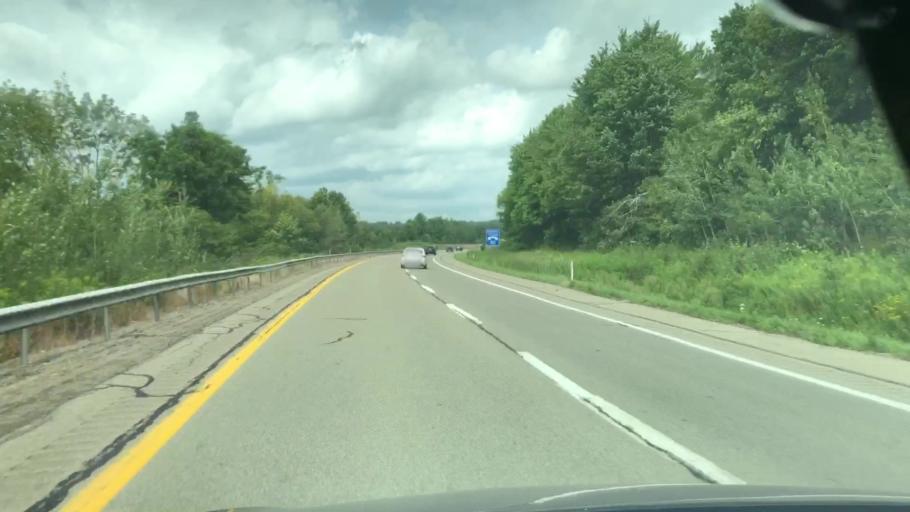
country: US
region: Pennsylvania
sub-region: Crawford County
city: Meadville
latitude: 41.7257
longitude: -80.2049
